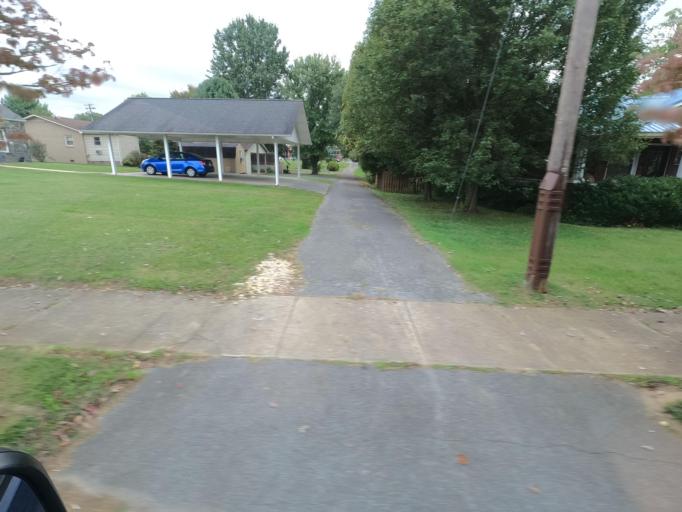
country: US
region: Tennessee
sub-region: Carter County
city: Elizabethton
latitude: 36.3457
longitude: -82.2231
